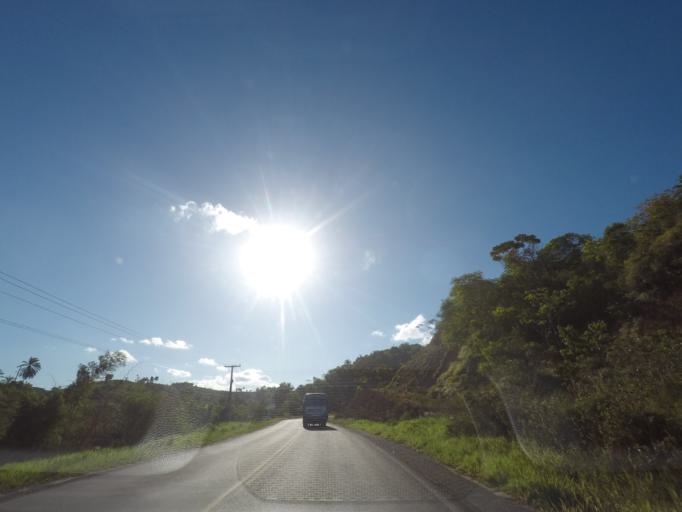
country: BR
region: Bahia
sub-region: Nazare
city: Nazare
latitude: -13.0414
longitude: -39.0121
